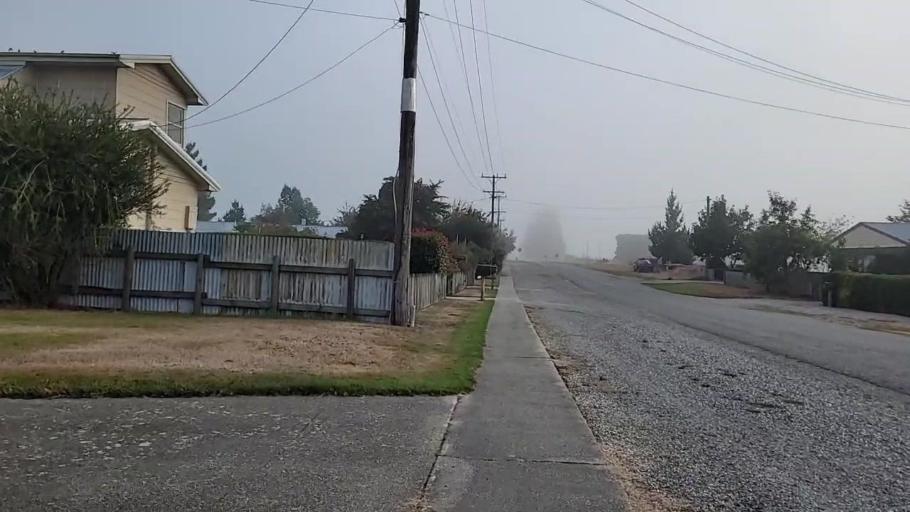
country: NZ
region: Southland
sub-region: Gore District
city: Gore
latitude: -45.6318
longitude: 169.3616
